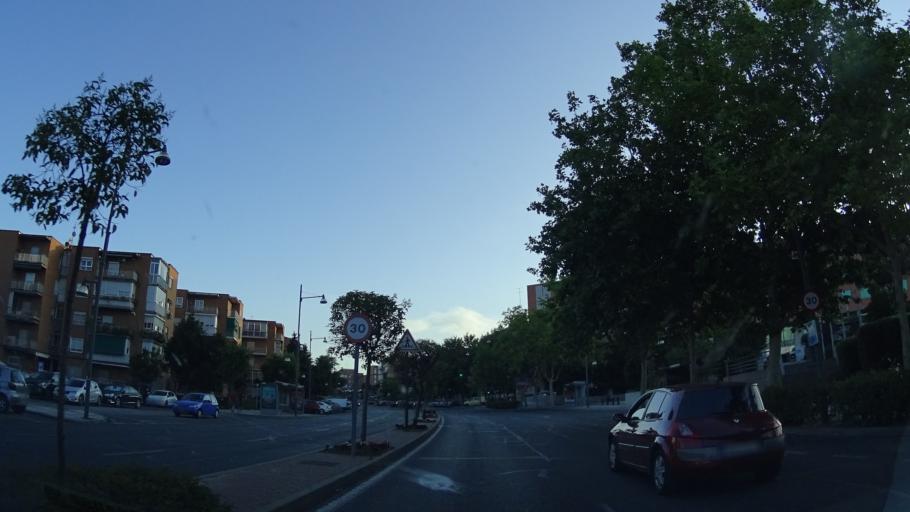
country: ES
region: Madrid
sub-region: Provincia de Madrid
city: Alcobendas
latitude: 40.5474
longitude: -3.6406
